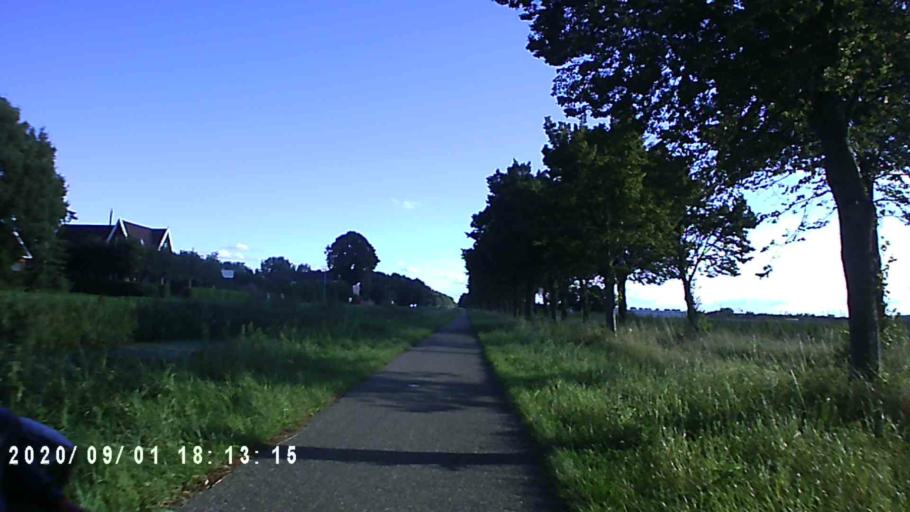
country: NL
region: Groningen
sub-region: Gemeente Hoogezand-Sappemeer
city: Sappemeer
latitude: 53.1841
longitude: 6.7859
